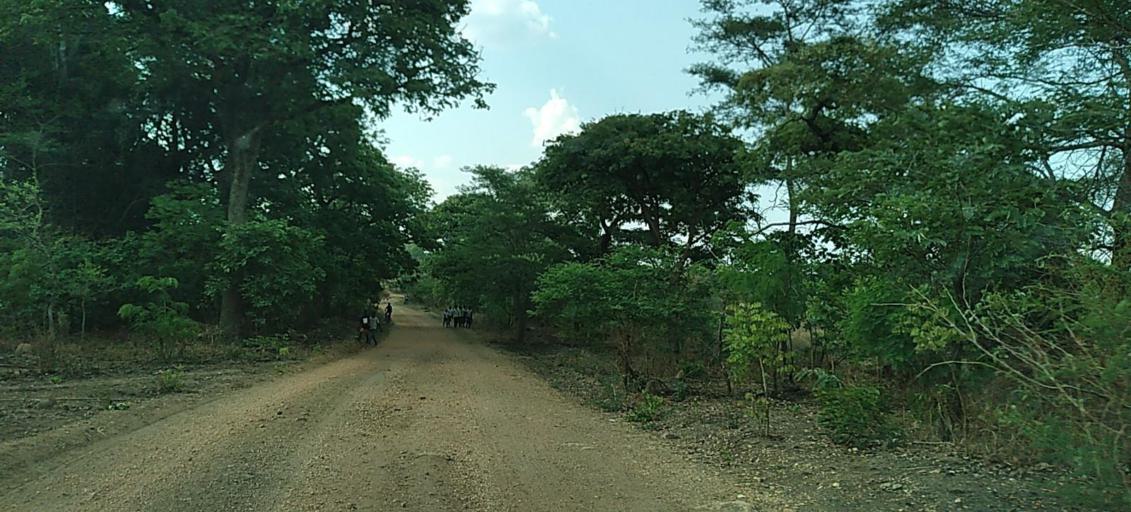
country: ZM
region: Copperbelt
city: Mpongwe
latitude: -13.4815
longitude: 28.0843
